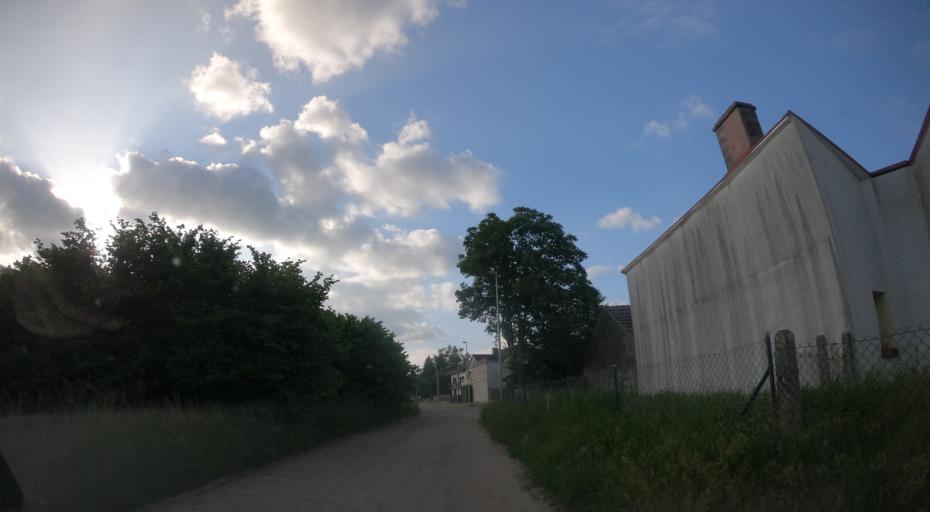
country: PL
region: Lubusz
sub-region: Powiat gorzowski
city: Santok
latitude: 52.7426
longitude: 15.3959
